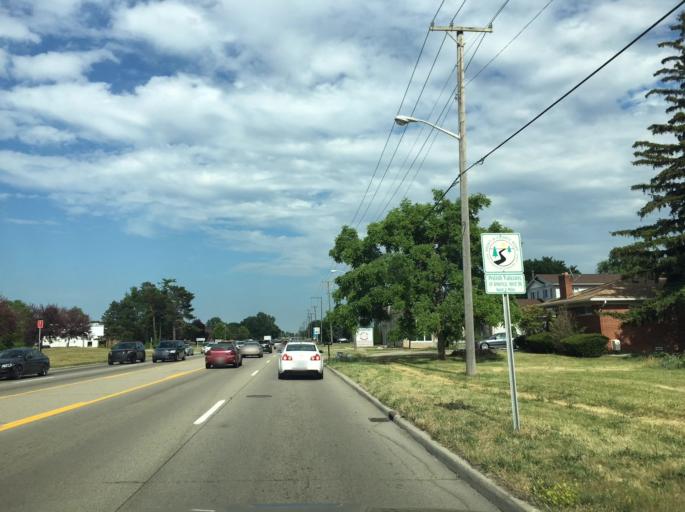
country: US
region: Michigan
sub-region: Macomb County
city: Sterling Heights
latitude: 42.5361
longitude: -83.0469
